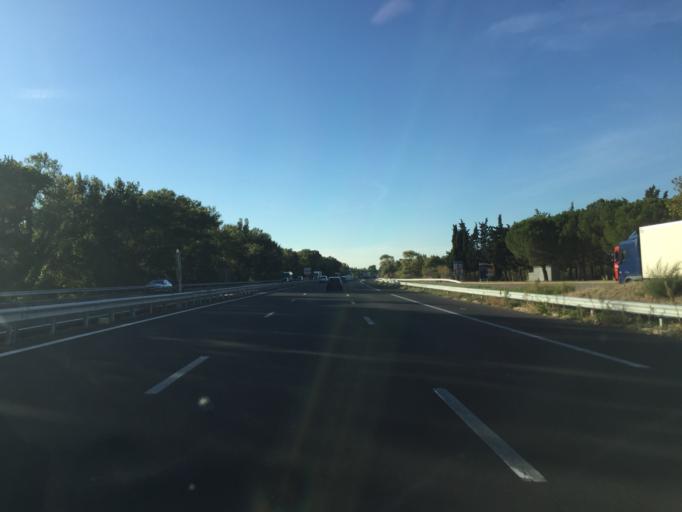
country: FR
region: Provence-Alpes-Cote d'Azur
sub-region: Departement du Vaucluse
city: Cavaillon
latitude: 43.8318
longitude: 5.0094
